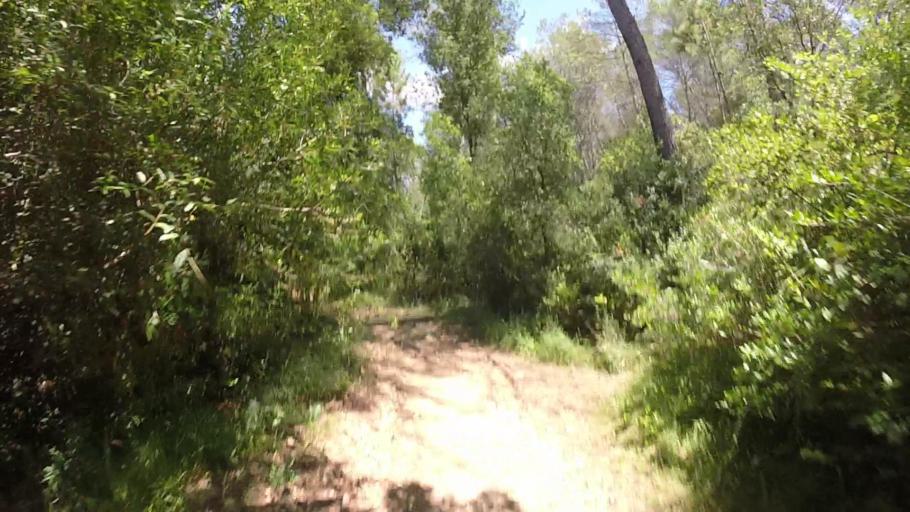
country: FR
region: Provence-Alpes-Cote d'Azur
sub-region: Departement des Alpes-Maritimes
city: Mougins
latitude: 43.6081
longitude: 7.0368
